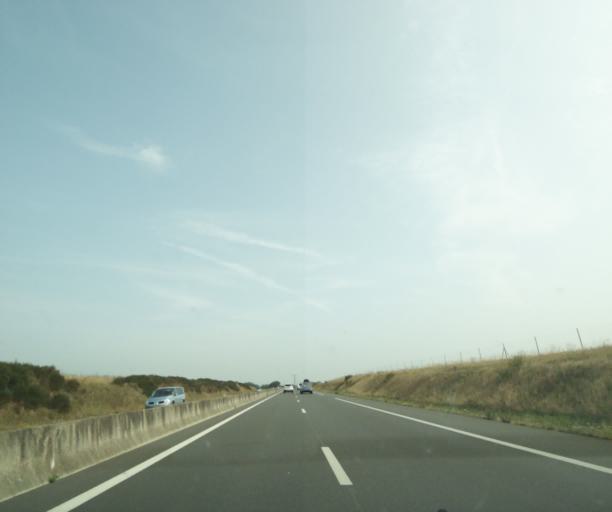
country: FR
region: Pays de la Loire
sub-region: Departement de la Sarthe
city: Arconnay
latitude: 48.3621
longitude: 0.0985
